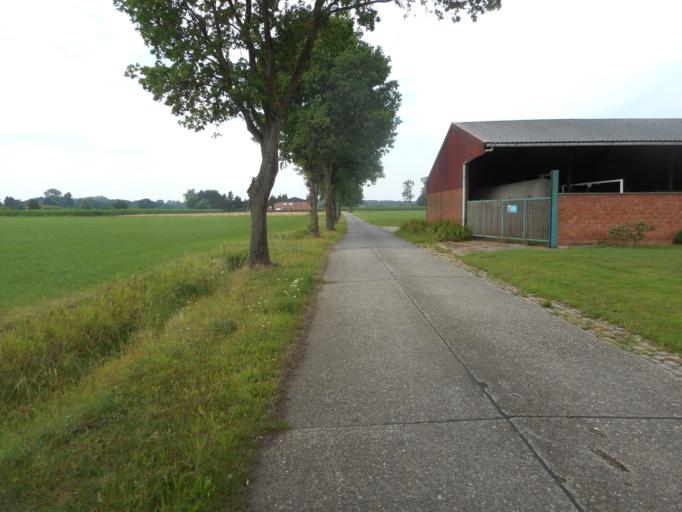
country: BE
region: Flanders
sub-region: Provincie Antwerpen
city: Herenthout
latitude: 51.1070
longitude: 4.7698
